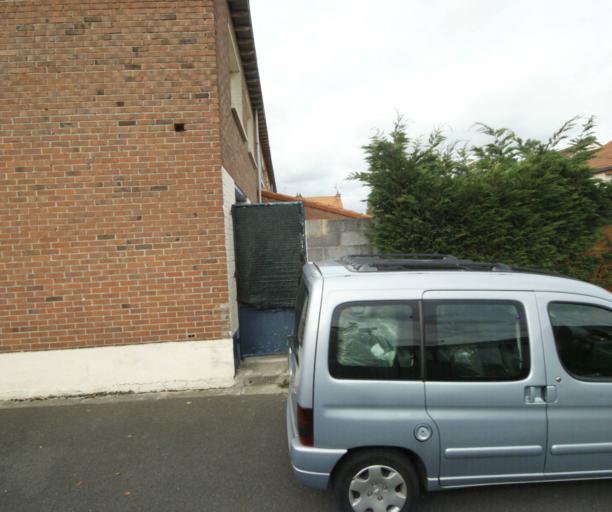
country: FR
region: Nord-Pas-de-Calais
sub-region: Departement du Nord
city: Erquinghem-Lys
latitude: 50.6781
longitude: 2.8605
